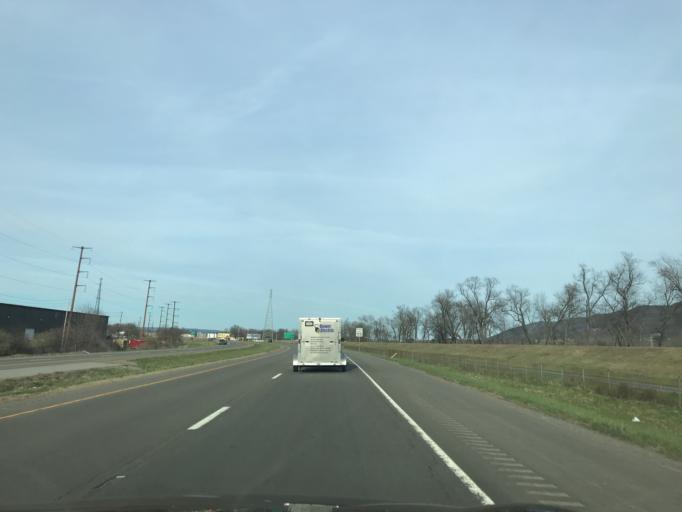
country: US
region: Pennsylvania
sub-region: Lycoming County
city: Duboistown
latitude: 41.2248
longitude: -77.0549
